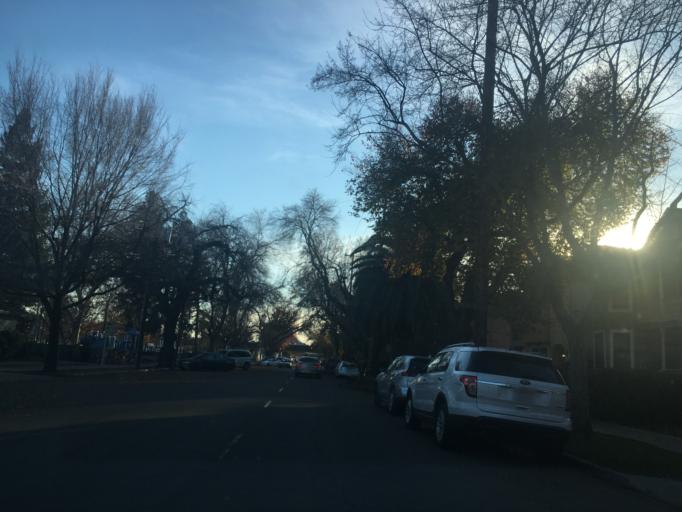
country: US
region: California
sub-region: Sacramento County
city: Sacramento
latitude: 38.5695
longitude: -121.5042
